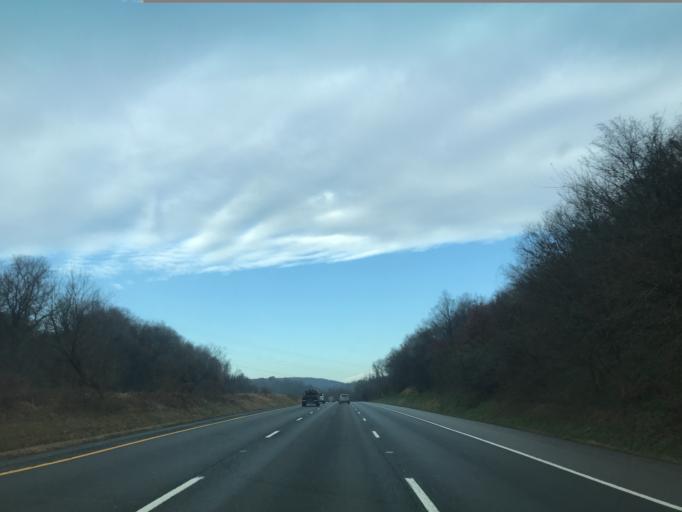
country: US
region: Maryland
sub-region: Frederick County
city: Myersville
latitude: 39.5037
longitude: -77.5787
